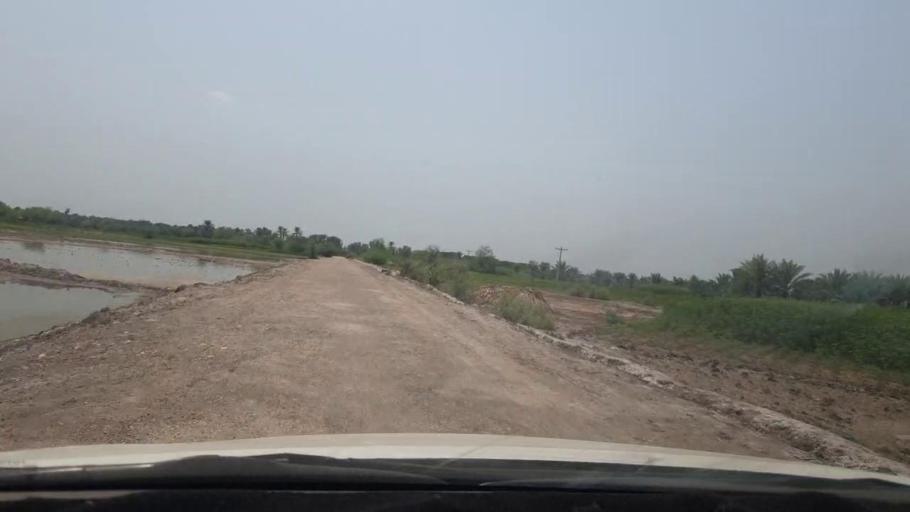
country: PK
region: Sindh
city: Khairpur
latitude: 27.5116
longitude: 68.8158
